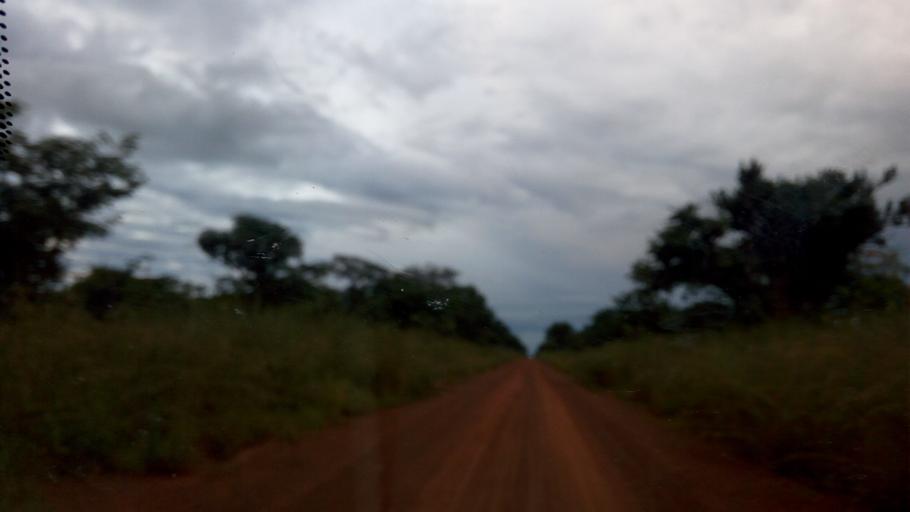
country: ZM
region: Luapula
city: Mwense
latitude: -9.9357
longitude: 28.1002
